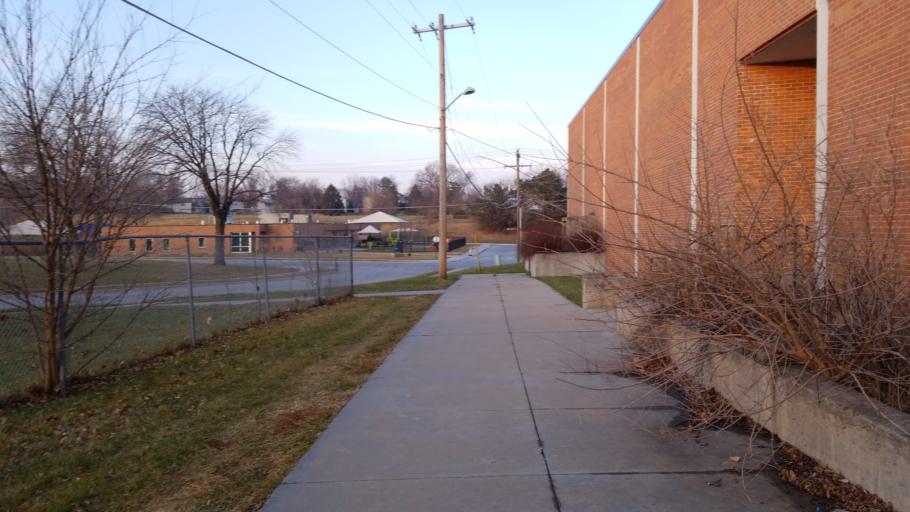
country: US
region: Nebraska
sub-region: Sarpy County
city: Offutt Air Force Base
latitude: 41.1285
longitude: -95.9487
